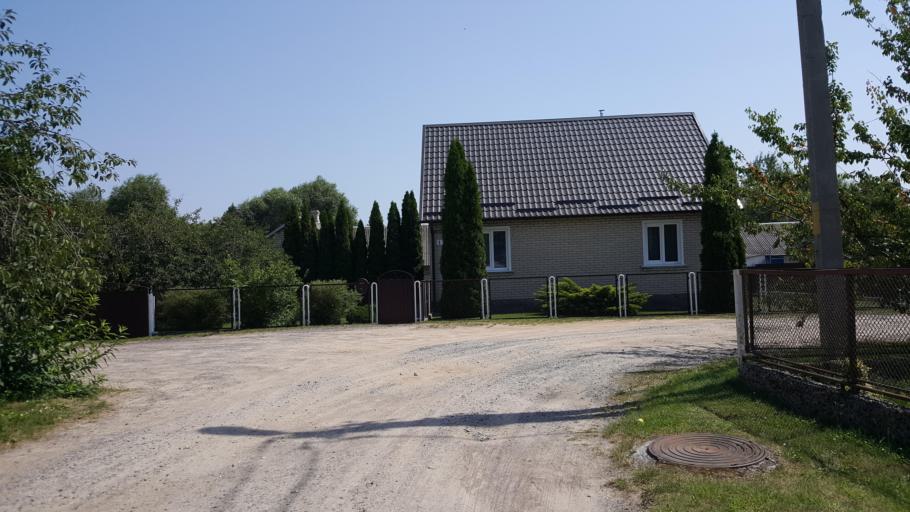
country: BY
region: Brest
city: Zhabinka
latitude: 52.1908
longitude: 24.0057
